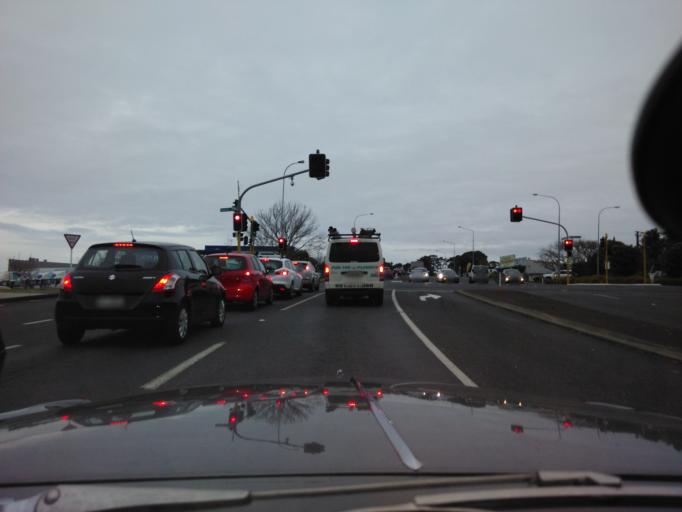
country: NZ
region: Auckland
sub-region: Auckland
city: Rothesay Bay
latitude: -36.7554
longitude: 174.7011
